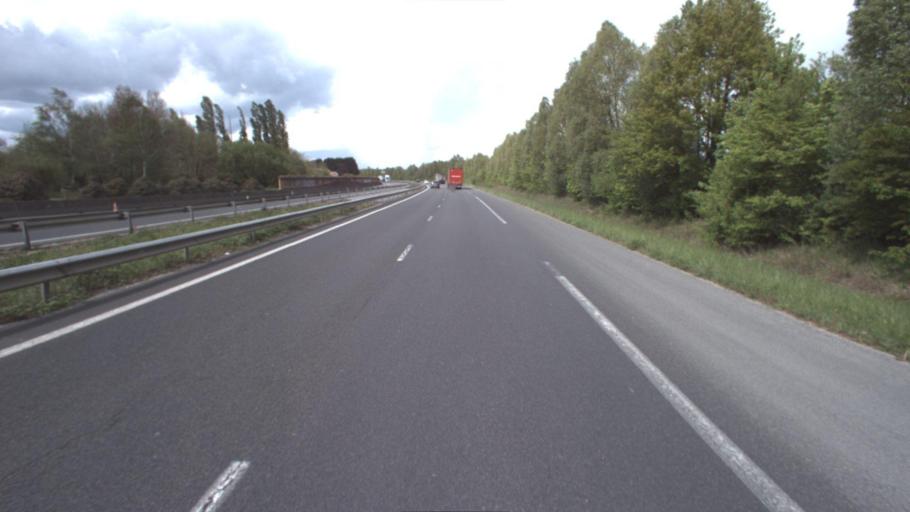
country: FR
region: Ile-de-France
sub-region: Departement de Seine-et-Marne
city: Fontenay-Tresigny
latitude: 48.7072
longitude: 2.8806
